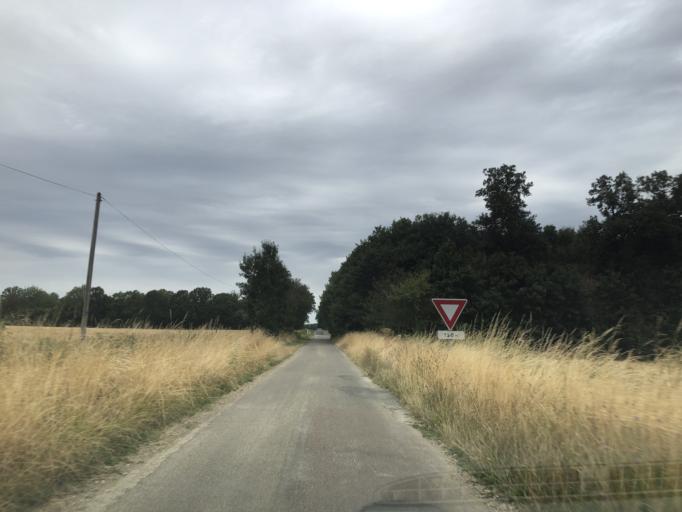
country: FR
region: Bourgogne
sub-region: Departement de l'Yonne
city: Aillant-sur-Tholon
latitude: 47.9181
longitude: 3.3098
